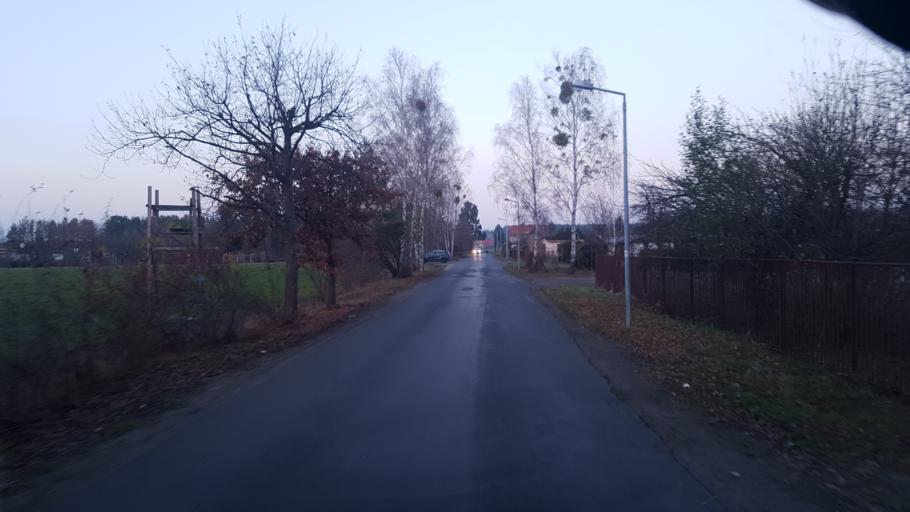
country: DE
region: Brandenburg
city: Lauchhammer
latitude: 51.5068
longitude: 13.7554
